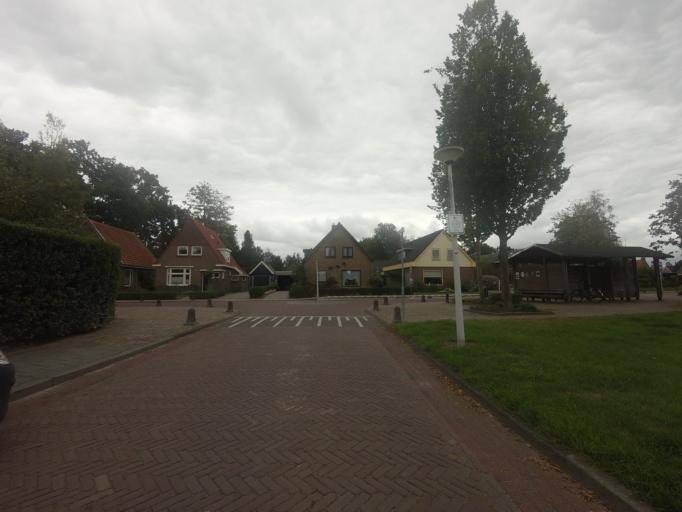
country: NL
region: Friesland
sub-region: Gemeente Weststellingwerf
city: Noordwolde
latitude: 52.9101
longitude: 6.2010
